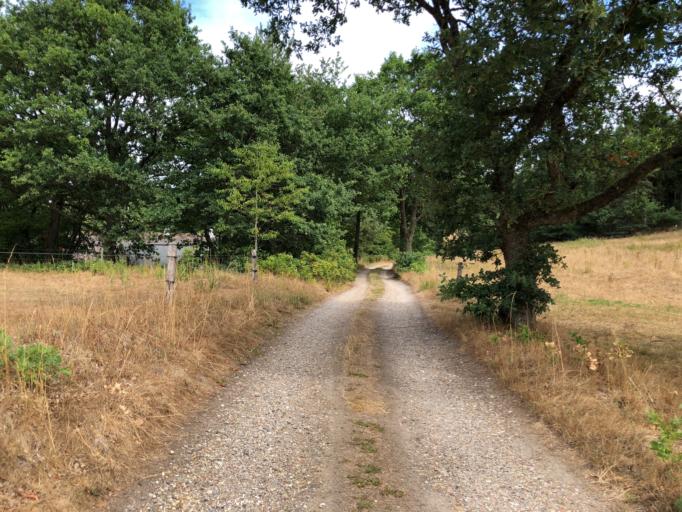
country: DK
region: South Denmark
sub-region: Vejle Kommune
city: Egtved
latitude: 55.6577
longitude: 9.2932
